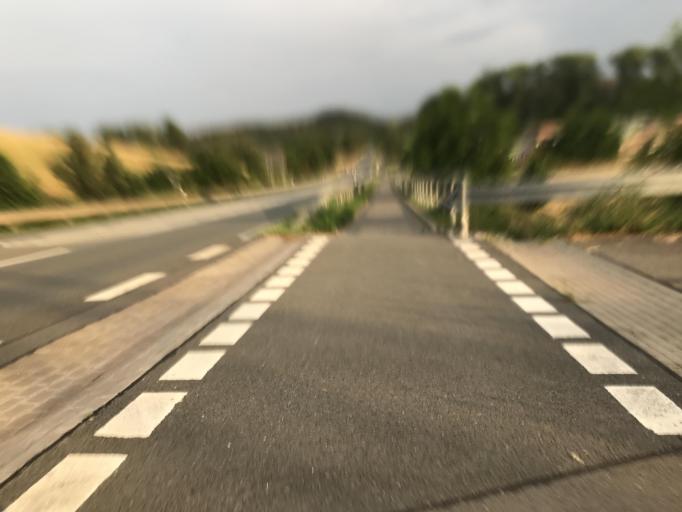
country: DE
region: Saxony-Anhalt
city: Quedlinburg
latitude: 51.8103
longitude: 11.1287
